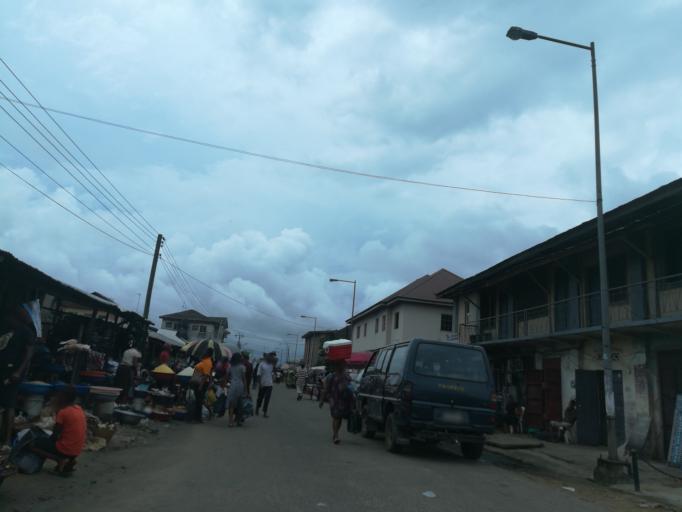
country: NG
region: Rivers
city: Port Harcourt
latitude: 4.7605
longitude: 7.0248
